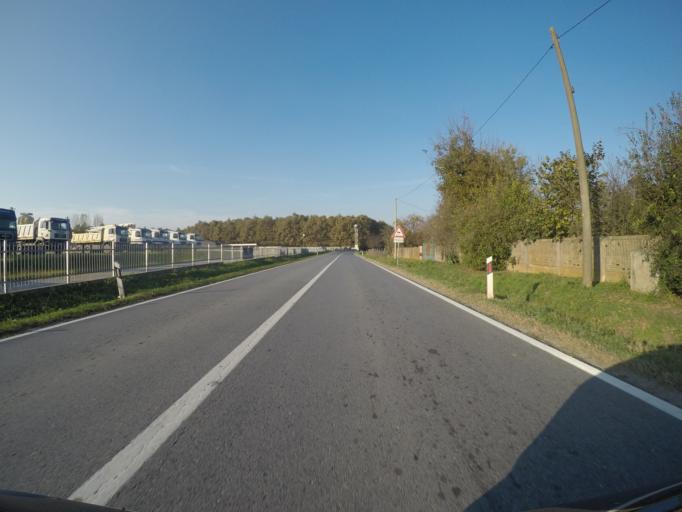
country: HR
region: Virovitick-Podravska
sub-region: Grad Virovitica
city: Virovitica
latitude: 45.8768
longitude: 17.4050
